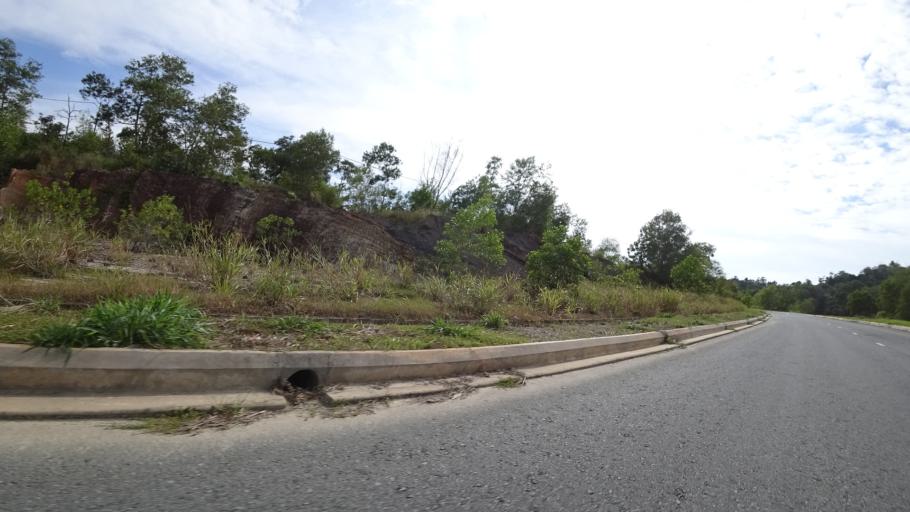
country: BN
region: Brunei and Muara
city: Bandar Seri Begawan
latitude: 4.9012
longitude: 114.7987
